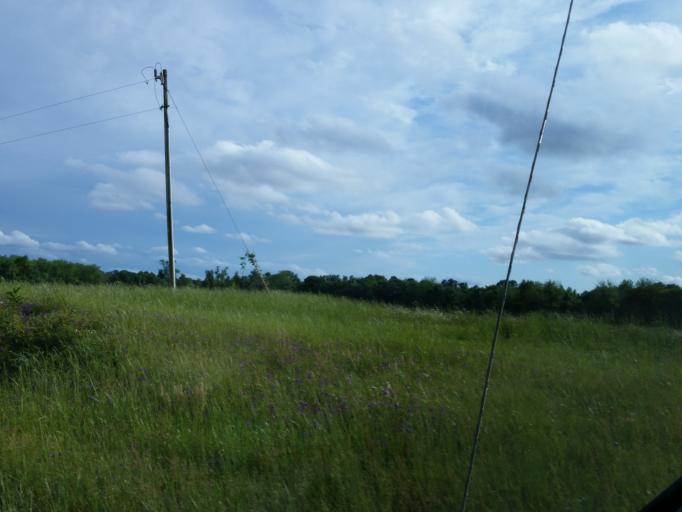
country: US
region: Georgia
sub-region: Dooly County
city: Vienna
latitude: 32.1669
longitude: -83.7650
